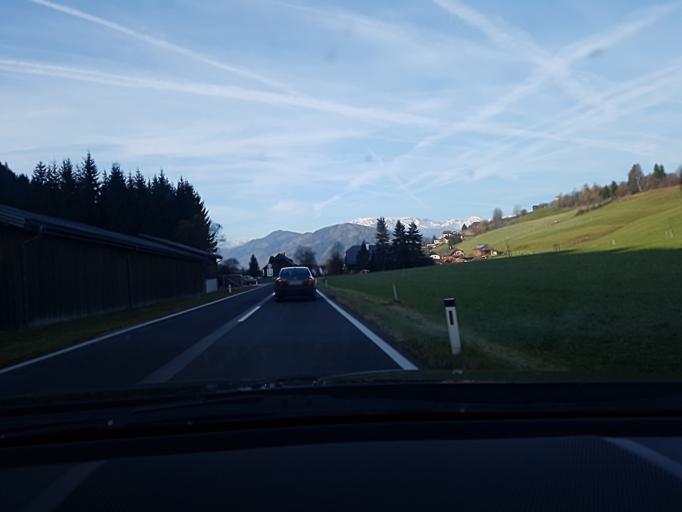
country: AT
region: Salzburg
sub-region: Politischer Bezirk Tamsweg
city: Tamsweg
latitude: 47.1316
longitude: 13.8255
